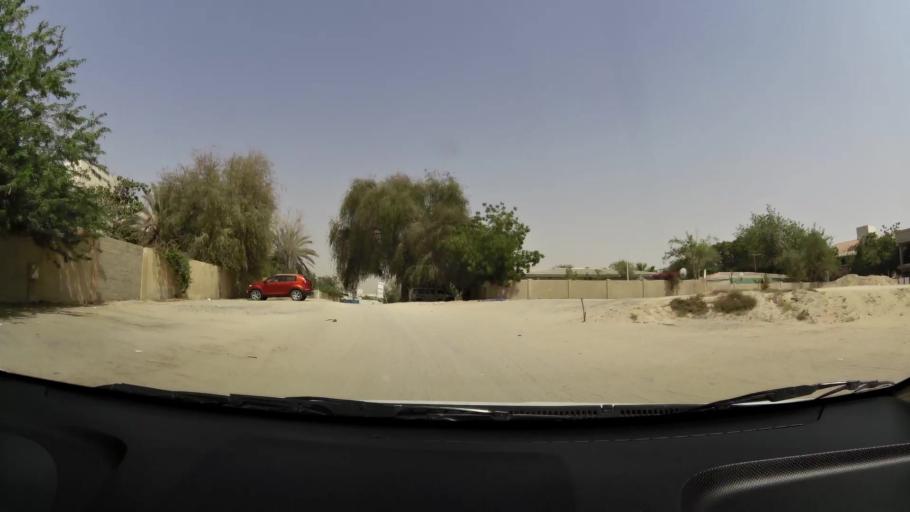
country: AE
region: Ash Shariqah
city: Sharjah
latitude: 25.3533
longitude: 55.4086
